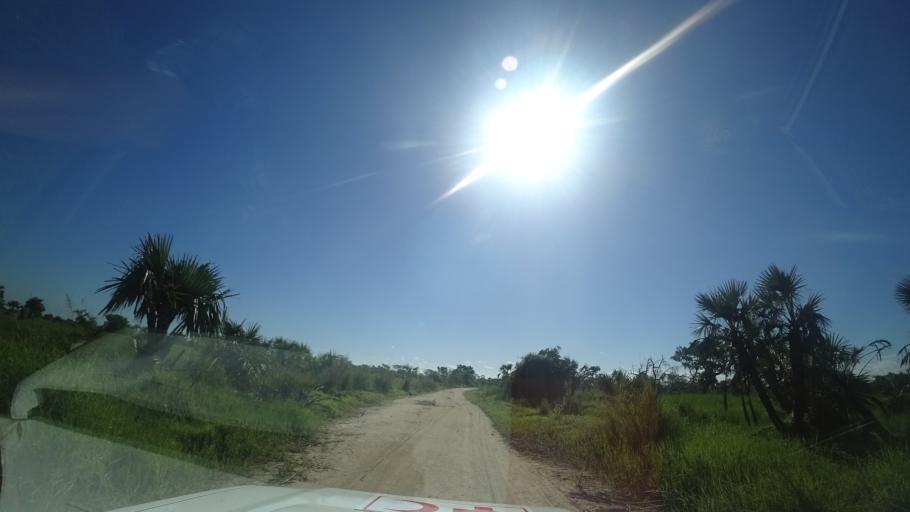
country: MZ
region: Sofala
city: Dondo
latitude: -19.3888
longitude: 34.5789
